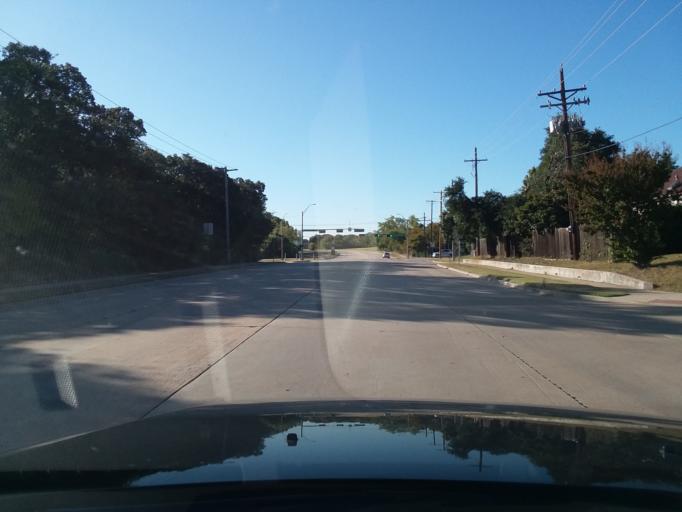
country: US
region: Texas
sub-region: Denton County
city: Lewisville
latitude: 33.0218
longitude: -97.0280
